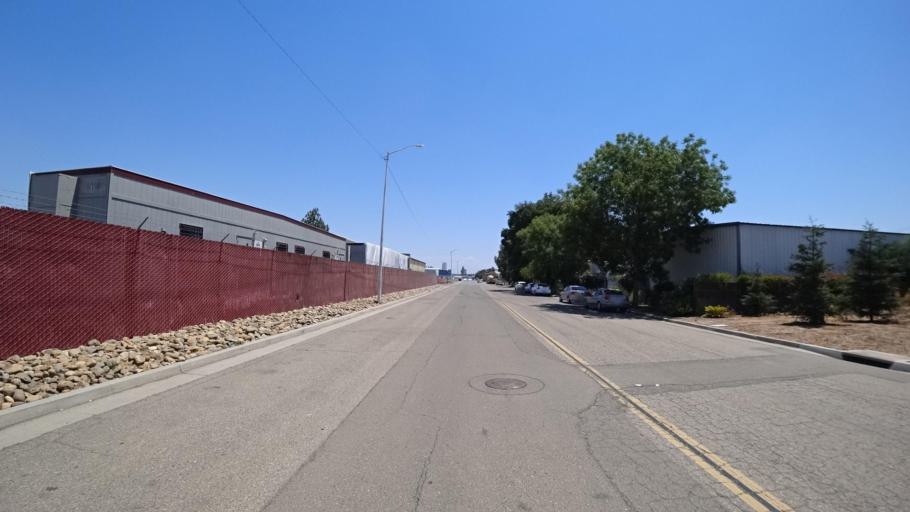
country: US
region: California
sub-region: Fresno County
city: Sunnyside
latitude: 36.7618
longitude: -119.7148
